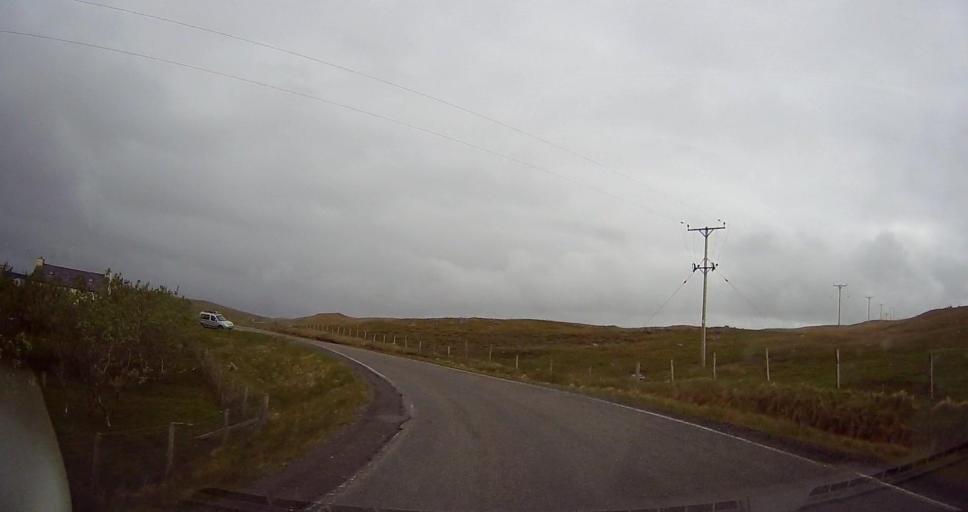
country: GB
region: Scotland
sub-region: Shetland Islands
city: Sandwick
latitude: 60.2329
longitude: -1.5536
